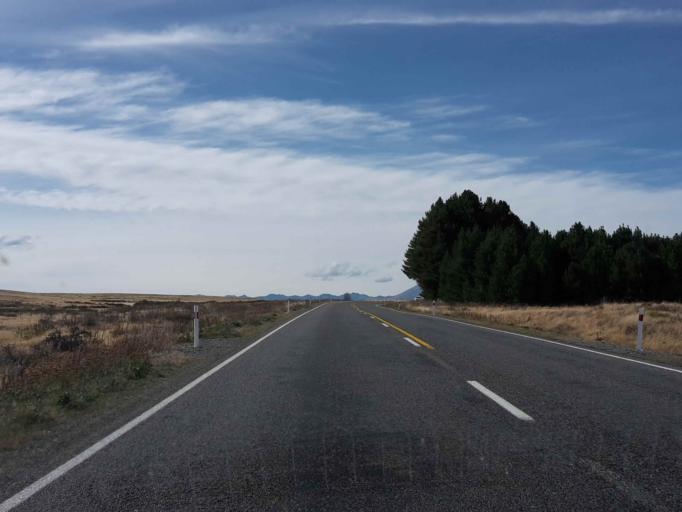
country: NZ
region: Canterbury
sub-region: Timaru District
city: Pleasant Point
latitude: -44.0341
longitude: 170.3881
